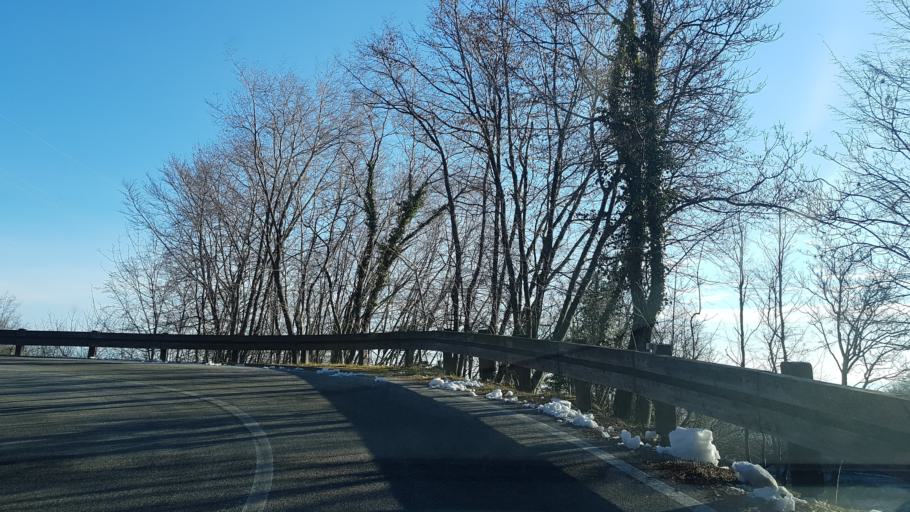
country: IT
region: Friuli Venezia Giulia
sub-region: Provincia di Udine
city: Forgaria nel Friuli
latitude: 46.2352
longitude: 12.9891
